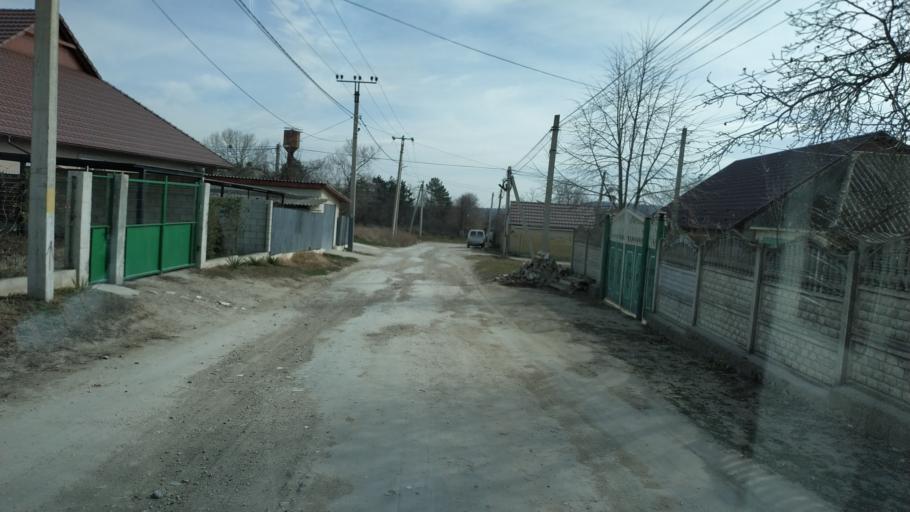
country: MD
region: Chisinau
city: Vatra
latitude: 47.0965
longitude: 28.6740
